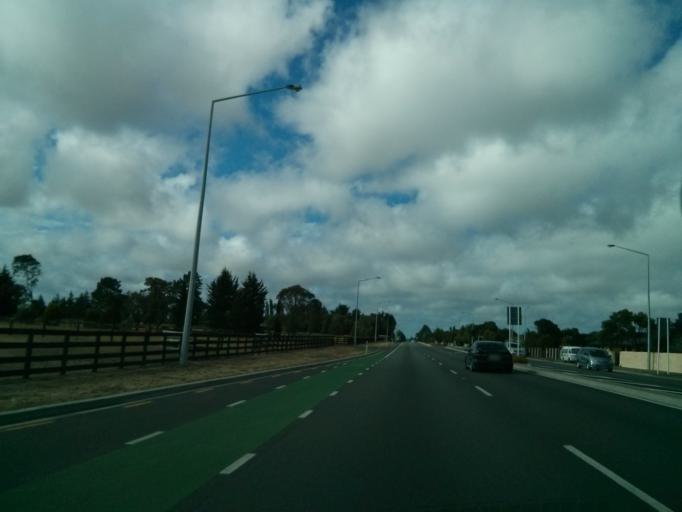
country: NZ
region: Canterbury
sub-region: Selwyn District
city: Prebbleton
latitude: -43.5186
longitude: 172.5351
